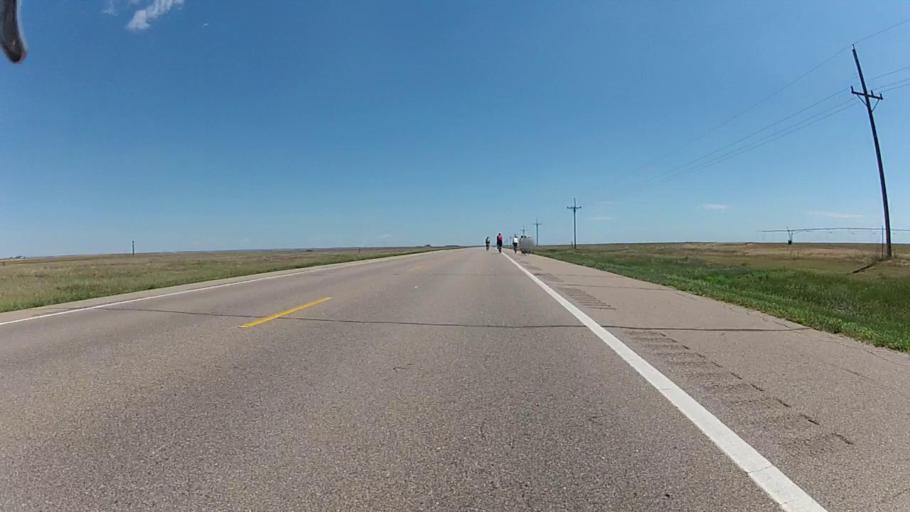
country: US
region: Kansas
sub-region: Ford County
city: Dodge City
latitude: 37.6782
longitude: -100.1861
